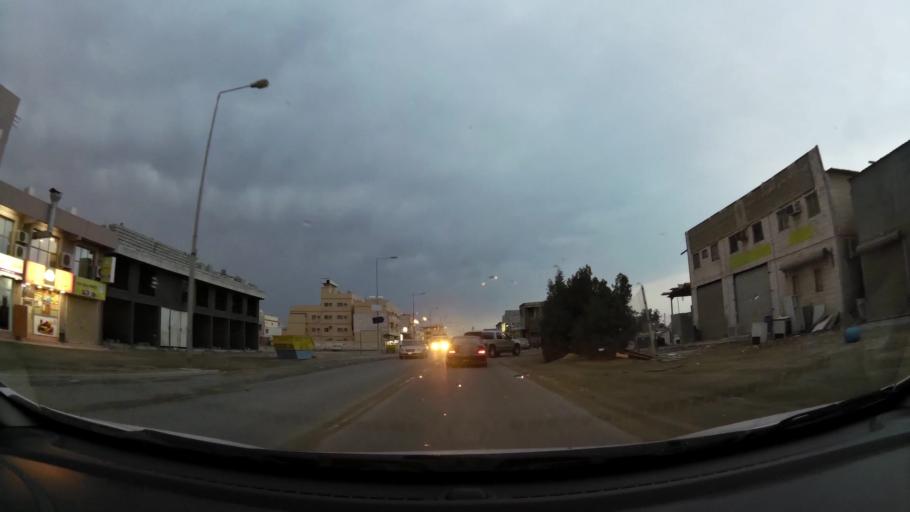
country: BH
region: Central Governorate
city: Madinat Hamad
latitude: 26.1486
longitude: 50.5027
